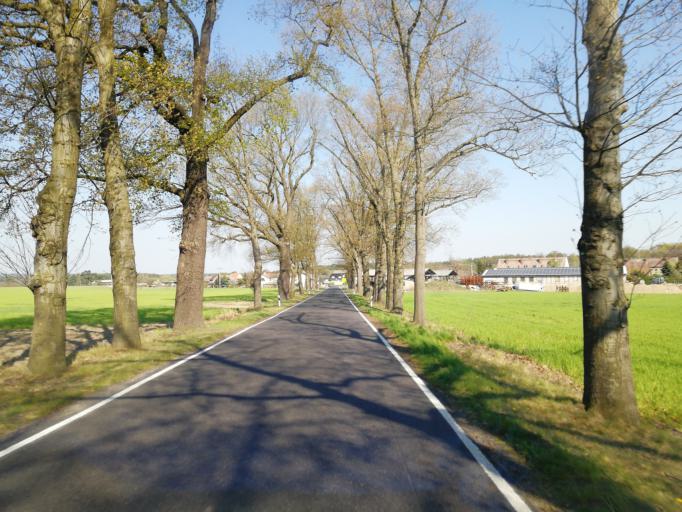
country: DE
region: Brandenburg
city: Bronkow
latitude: 51.7192
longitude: 13.8605
